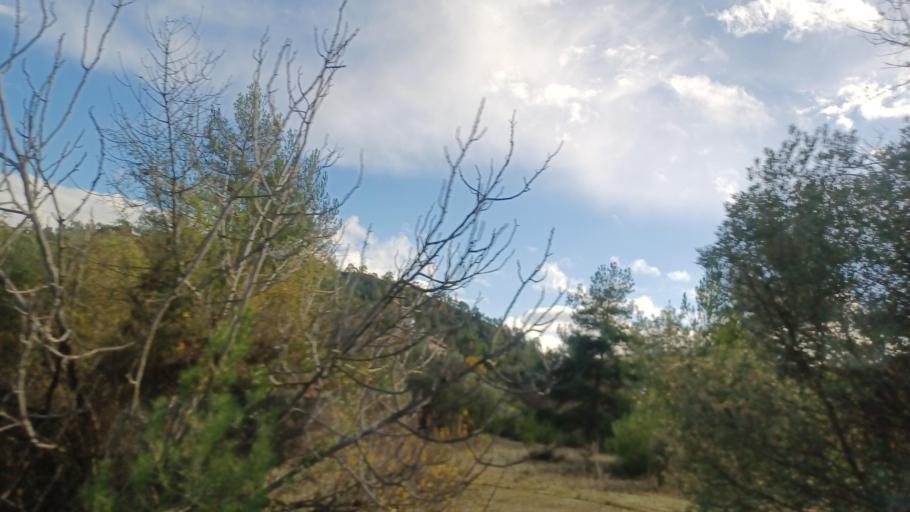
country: CY
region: Lefkosia
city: Lythrodontas
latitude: 34.9280
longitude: 33.2980
